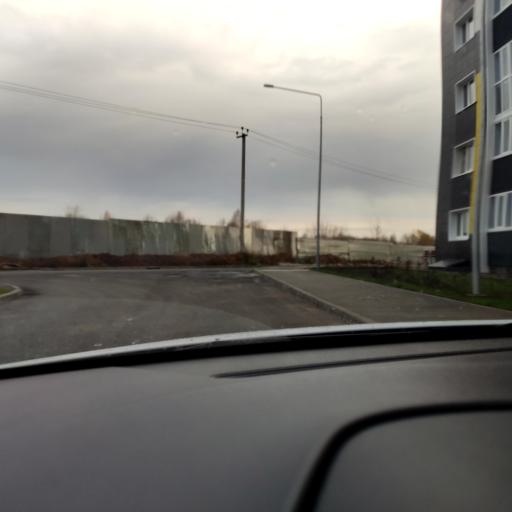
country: RU
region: Tatarstan
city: Osinovo
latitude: 55.8594
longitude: 48.9032
